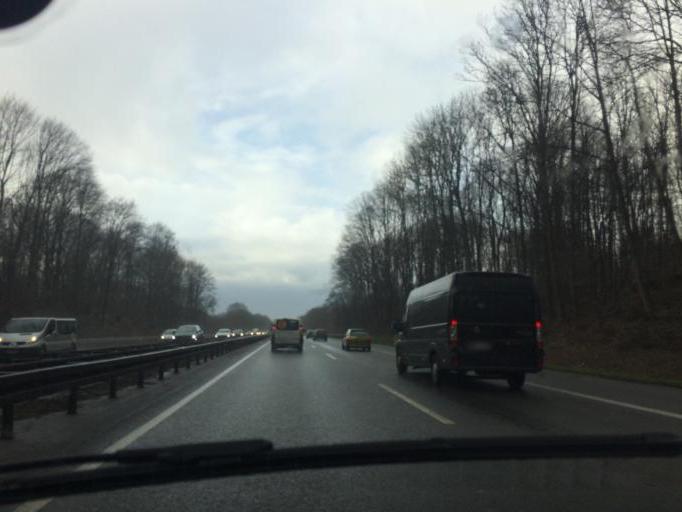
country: DE
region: North Rhine-Westphalia
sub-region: Regierungsbezirk Arnsberg
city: Herne
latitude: 51.5088
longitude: 7.2373
